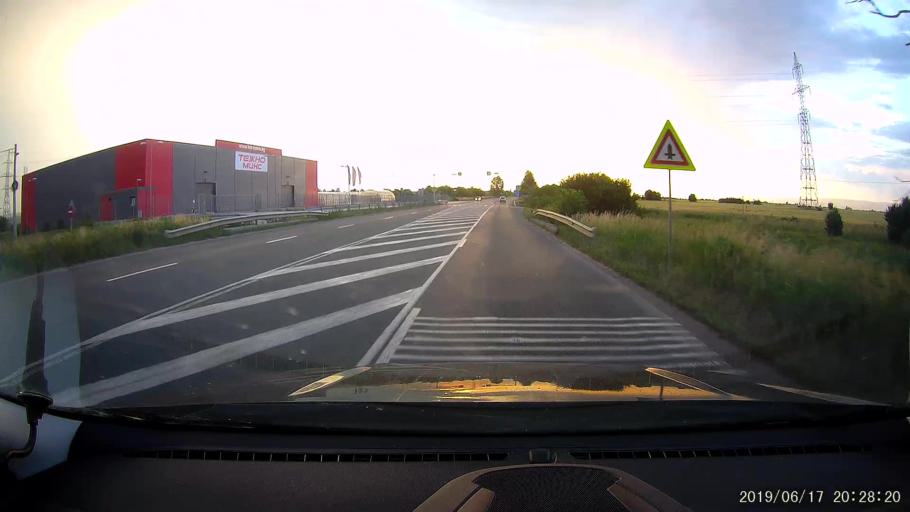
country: BG
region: Sofiya
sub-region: Obshtina Bozhurishte
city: Bozhurishte
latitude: 42.7770
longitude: 23.1788
